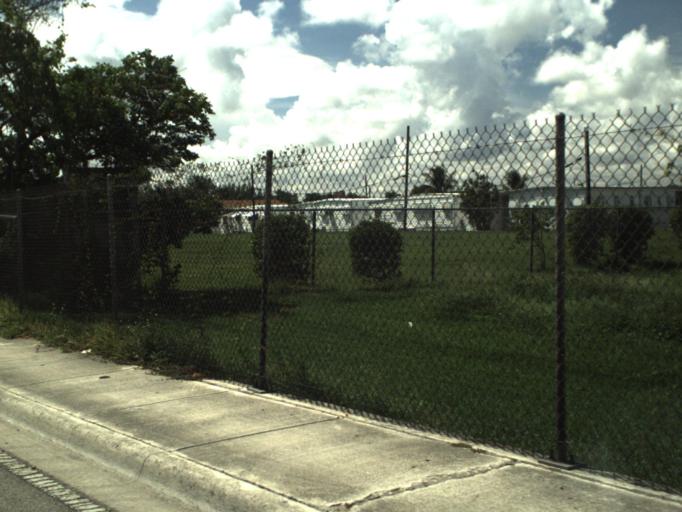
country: US
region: Florida
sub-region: Broward County
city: Pembroke Park
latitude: 25.9960
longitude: -80.1731
